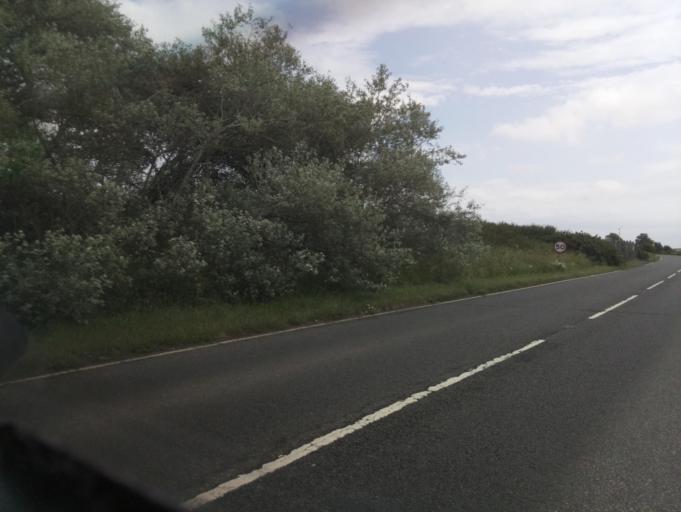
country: GB
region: Wales
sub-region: Vale of Glamorgan
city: Llantwit Major
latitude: 51.4024
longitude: -3.4515
